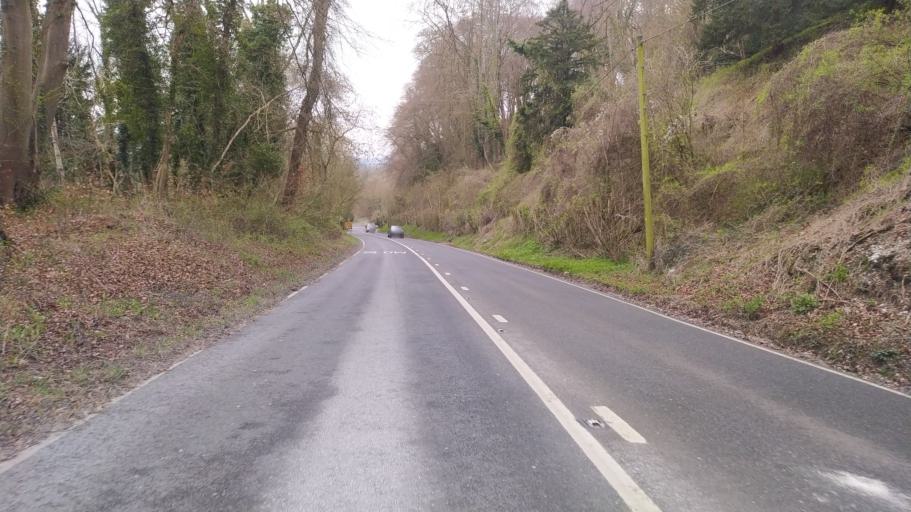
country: GB
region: England
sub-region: West Sussex
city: Petworth
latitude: 50.9369
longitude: -0.6384
